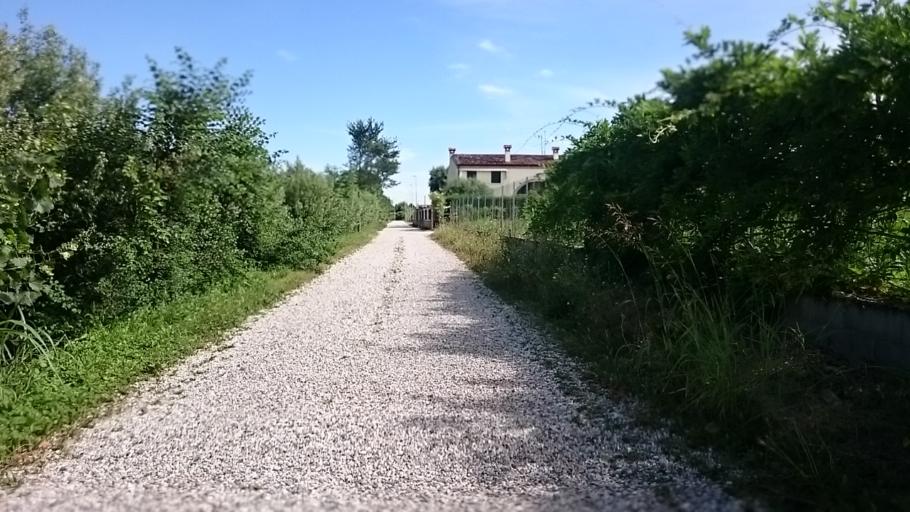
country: IT
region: Veneto
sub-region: Provincia di Padova
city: Albignasego
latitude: 45.3480
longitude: 11.8947
